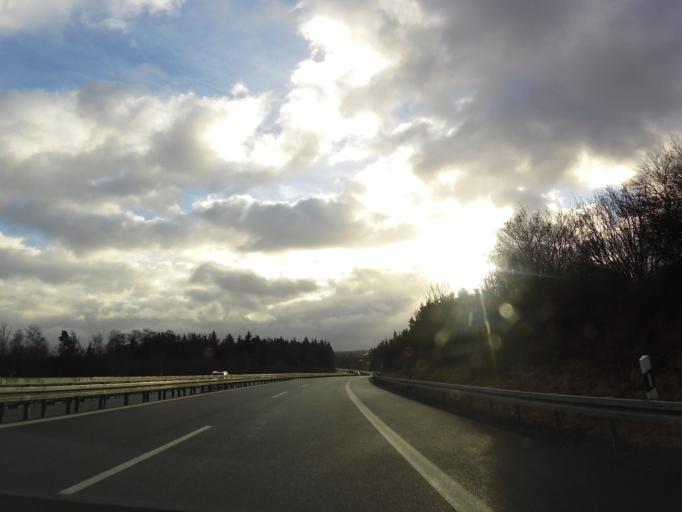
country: DE
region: Bavaria
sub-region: Upper Franconia
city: Thiersheim
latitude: 50.0818
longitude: 12.1041
